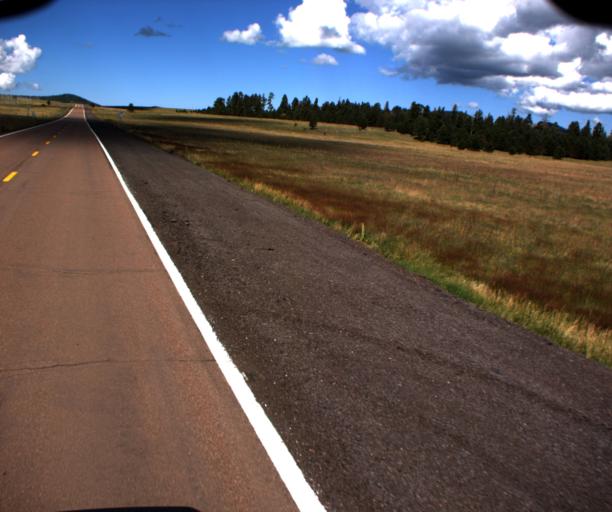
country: US
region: Arizona
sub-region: Apache County
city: Eagar
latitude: 34.0540
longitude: -109.5165
